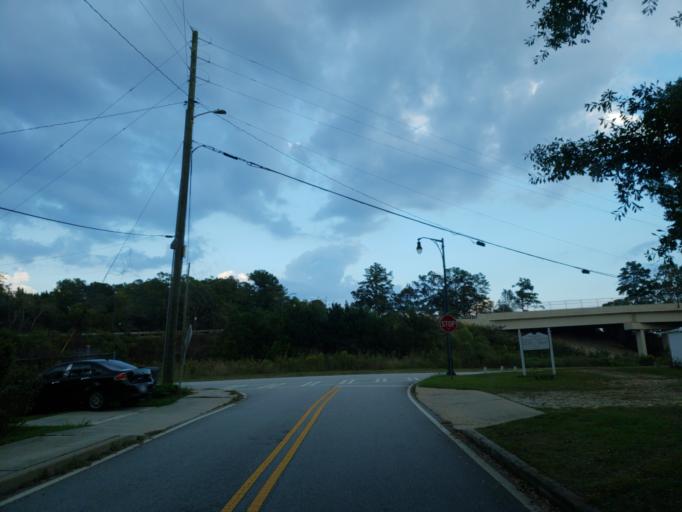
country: US
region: Georgia
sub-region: Cobb County
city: Powder Springs
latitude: 33.8545
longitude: -84.6834
